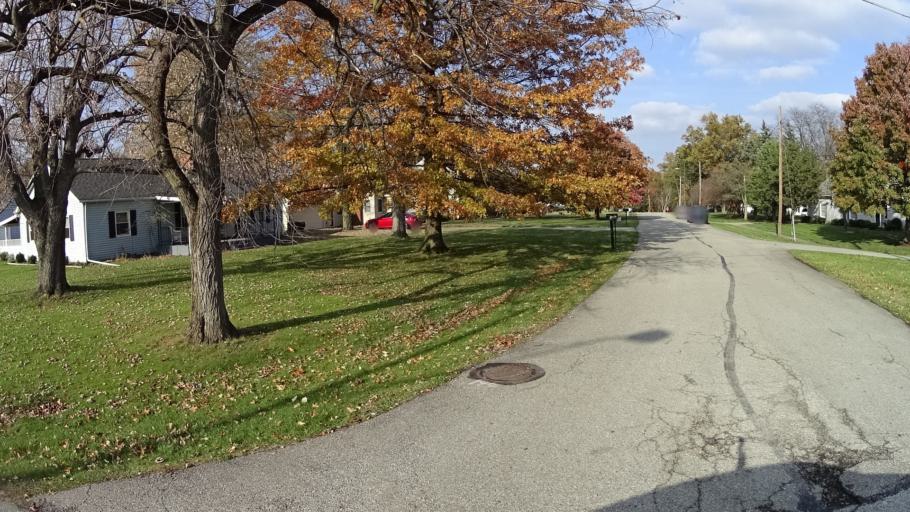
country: US
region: Ohio
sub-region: Lorain County
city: Elyria
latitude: 41.3897
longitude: -82.0909
